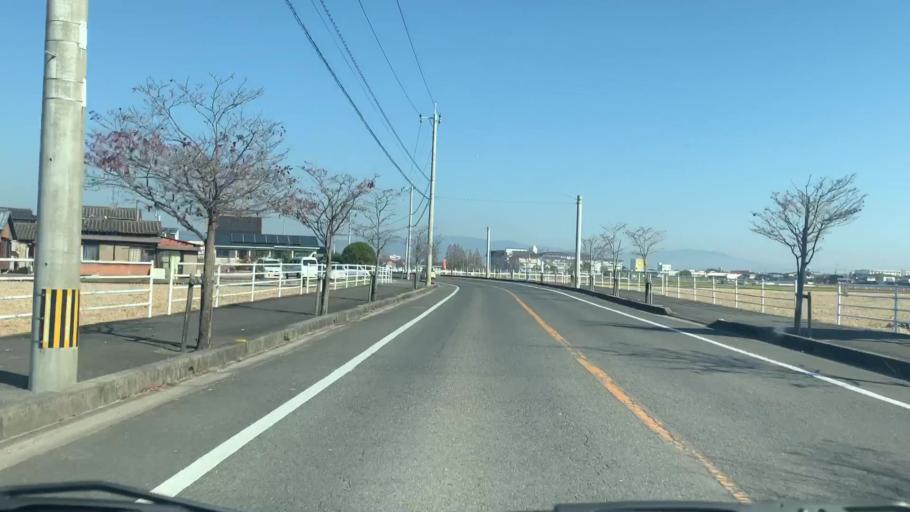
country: JP
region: Saga Prefecture
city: Saga-shi
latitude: 33.2329
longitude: 130.3127
